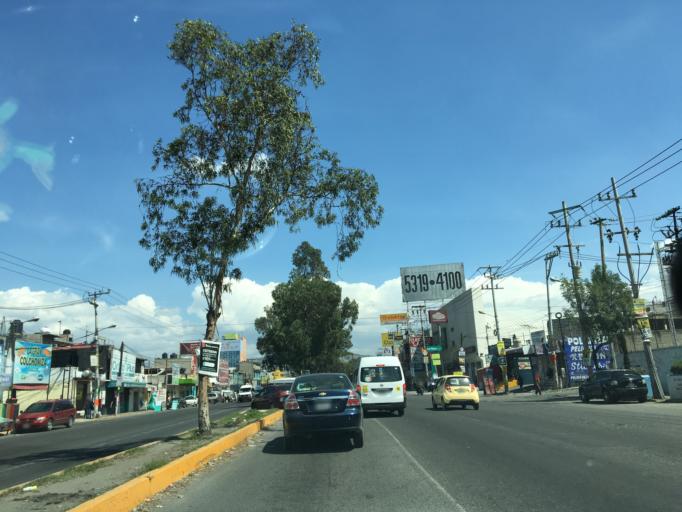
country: MX
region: Mexico
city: Los Reyes La Paz
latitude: 19.3560
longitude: -98.9820
